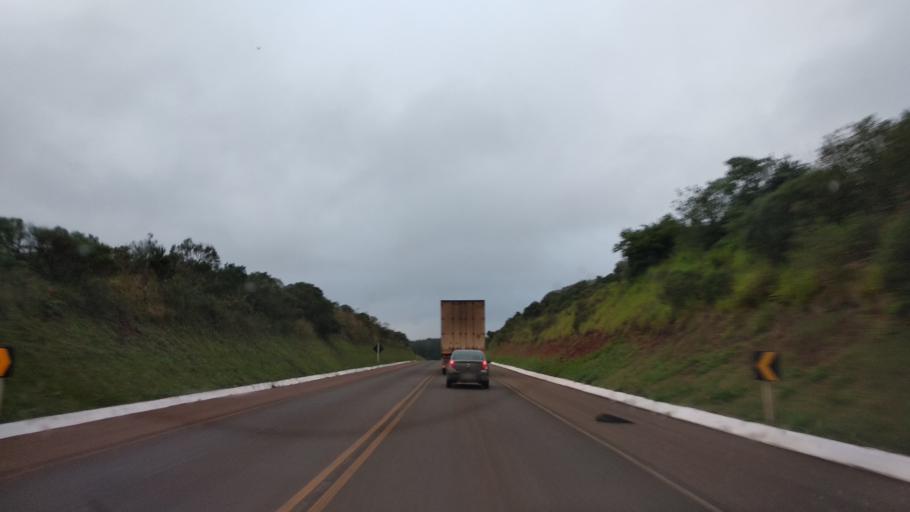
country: BR
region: Santa Catarina
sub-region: Campos Novos
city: Campos Novos
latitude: -27.3953
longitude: -51.0474
